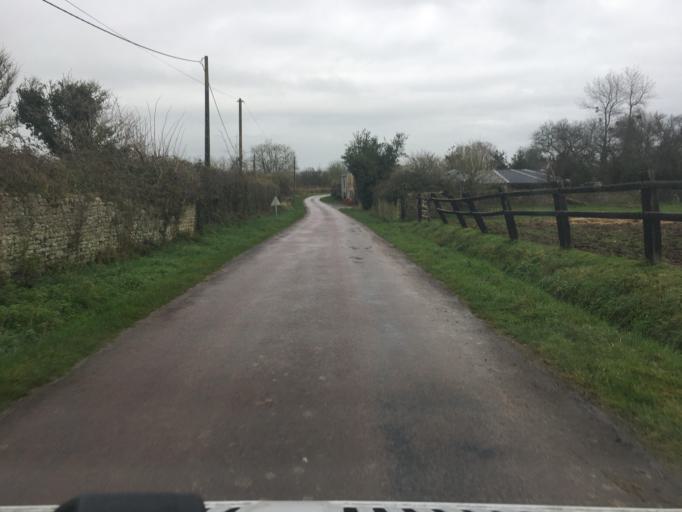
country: FR
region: Lower Normandy
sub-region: Departement de la Manche
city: Sainte-Mere-Eglise
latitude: 49.4405
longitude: -1.2514
